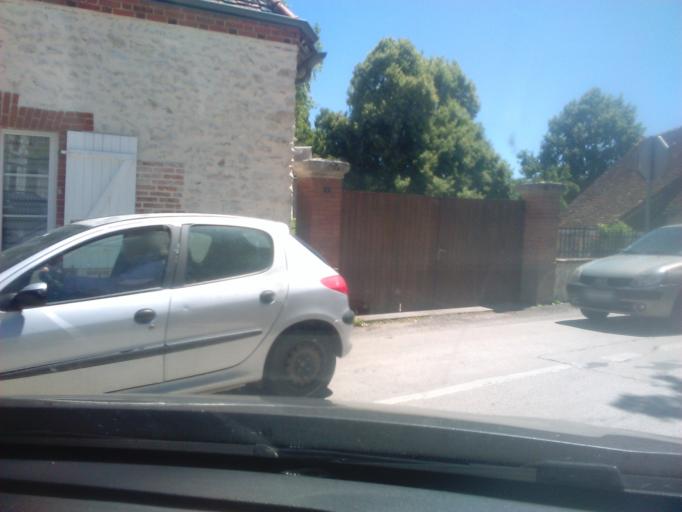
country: FR
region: Centre
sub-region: Departement du Loir-et-Cher
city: Saint-Sulpice-de-Pommeray
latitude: 47.6127
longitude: 1.2382
